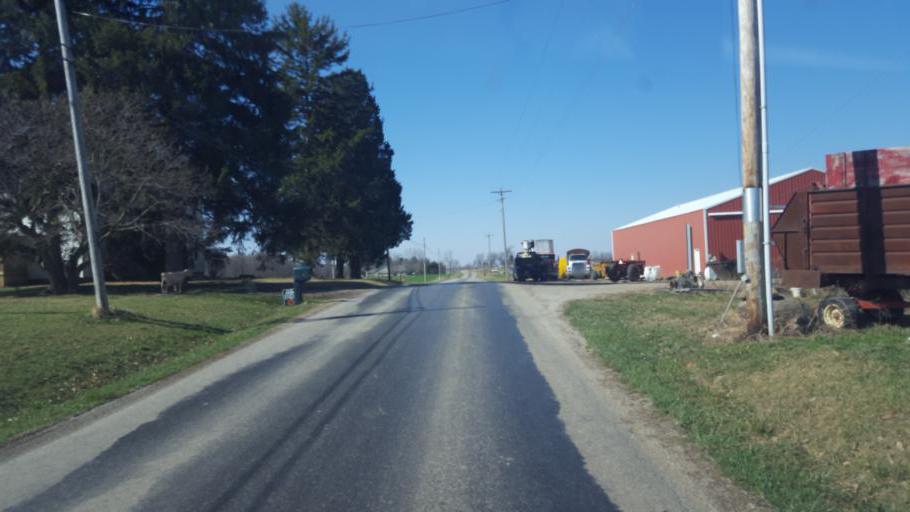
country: US
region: Ohio
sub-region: Morrow County
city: Mount Gilead
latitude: 40.5161
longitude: -82.8225
